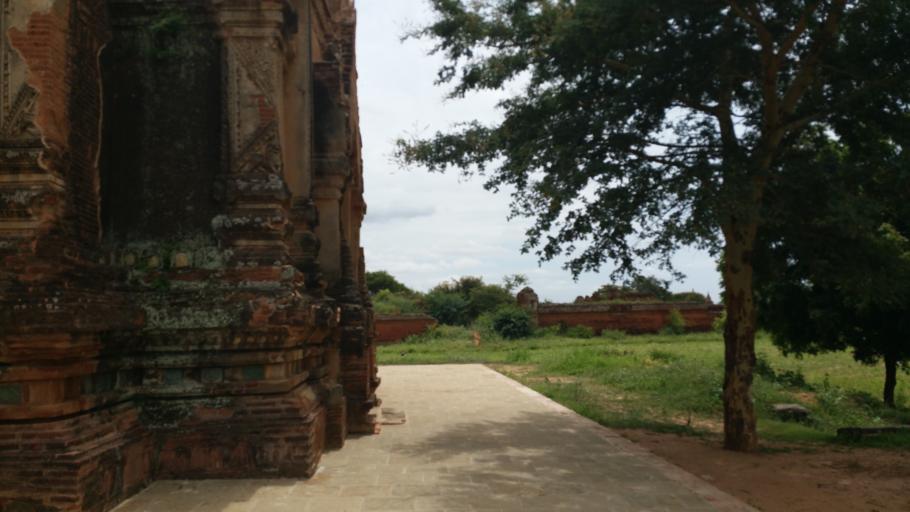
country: MM
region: Magway
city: Pakokku
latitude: 21.1629
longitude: 94.9006
